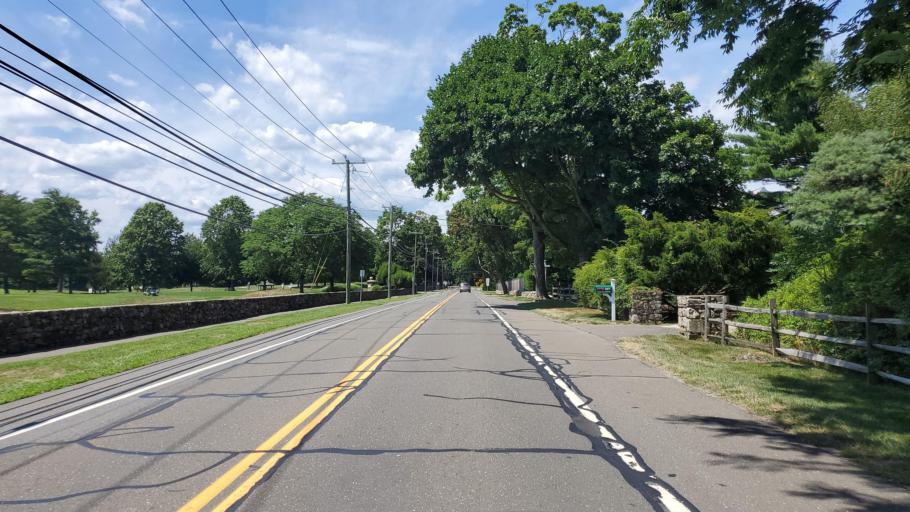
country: US
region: Connecticut
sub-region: Fairfield County
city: Westport
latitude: 41.1129
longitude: -73.3572
